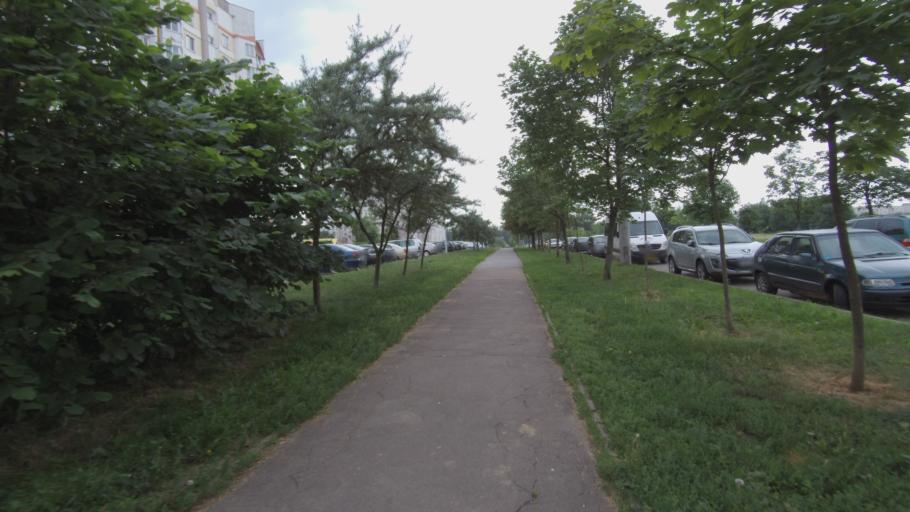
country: BY
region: Minsk
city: Syenitsa
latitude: 53.8494
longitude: 27.5635
